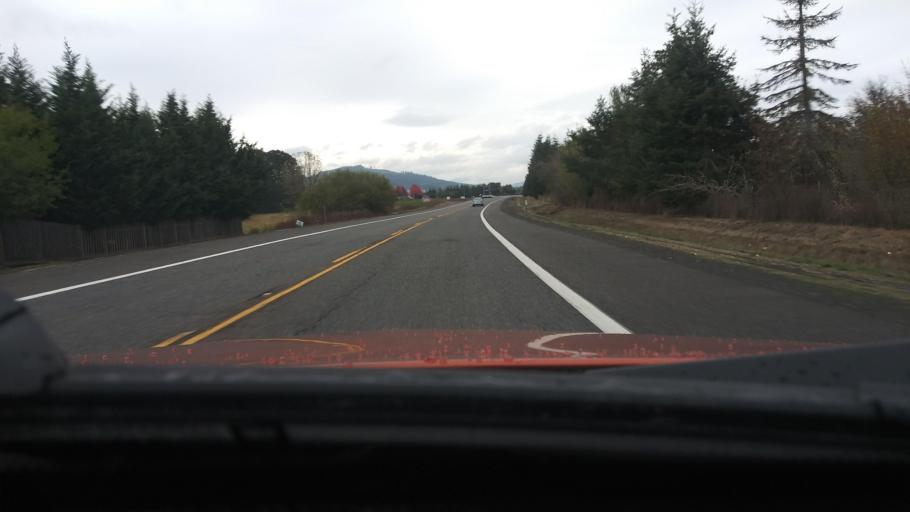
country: US
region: Oregon
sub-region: Washington County
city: Forest Grove
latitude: 45.5320
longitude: -123.1009
